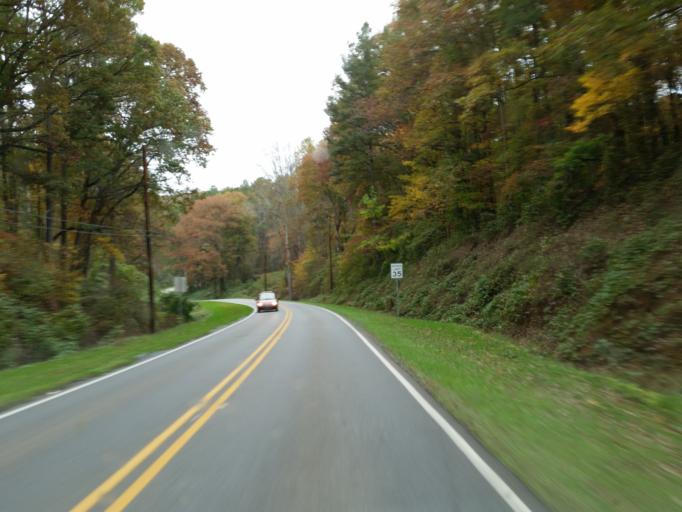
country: US
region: Georgia
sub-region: Pickens County
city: Jasper
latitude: 34.4771
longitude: -84.4226
